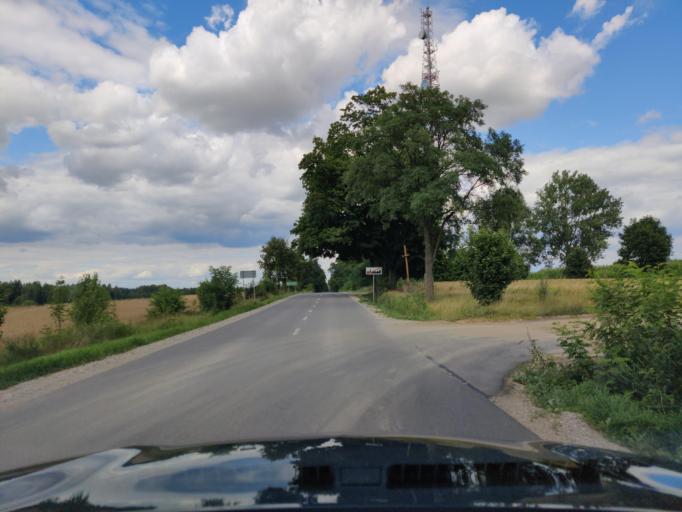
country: PL
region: Masovian Voivodeship
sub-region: Powiat sokolowski
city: Kosow Lacki
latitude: 52.5452
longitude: 22.0966
